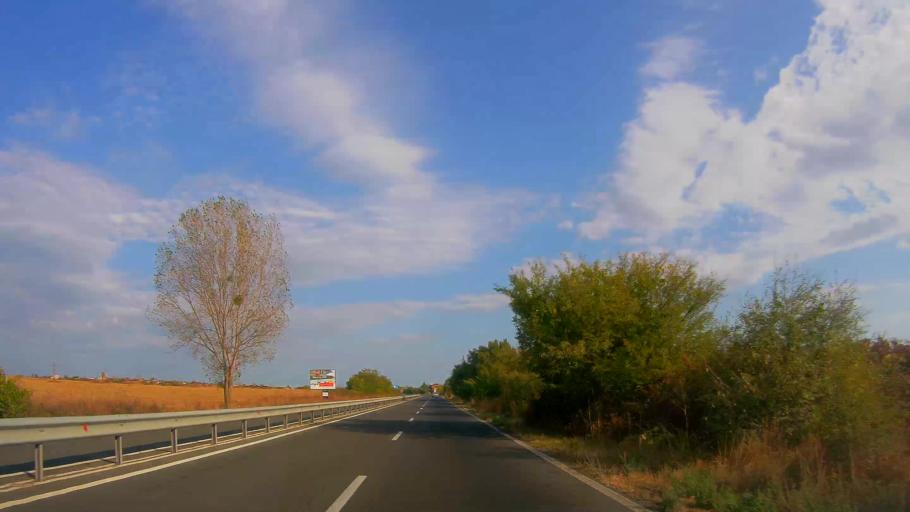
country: BG
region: Burgas
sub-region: Obshtina Sozopol
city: Chernomorets
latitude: 42.4277
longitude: 27.6403
